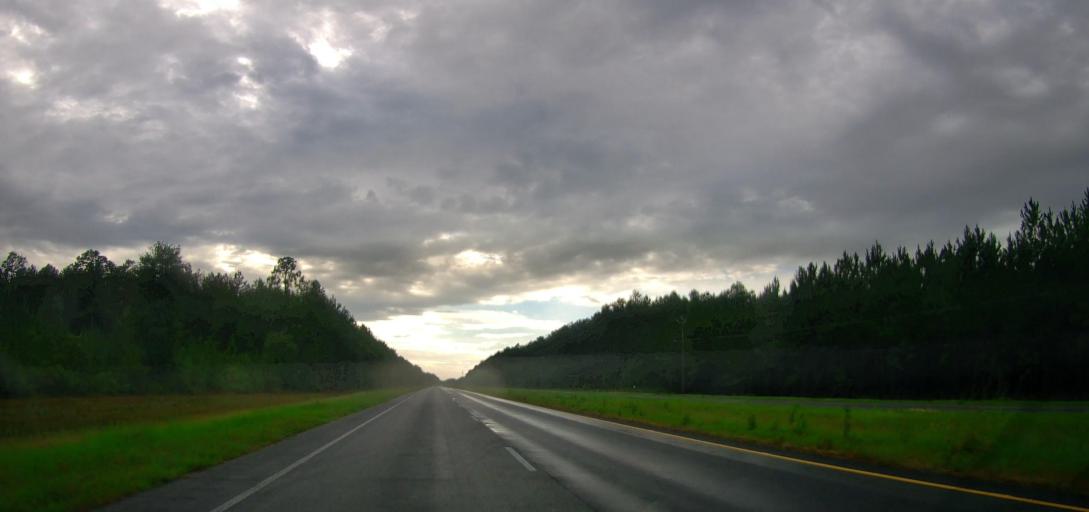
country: US
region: Georgia
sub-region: Ware County
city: Deenwood
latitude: 31.2589
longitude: -82.5036
